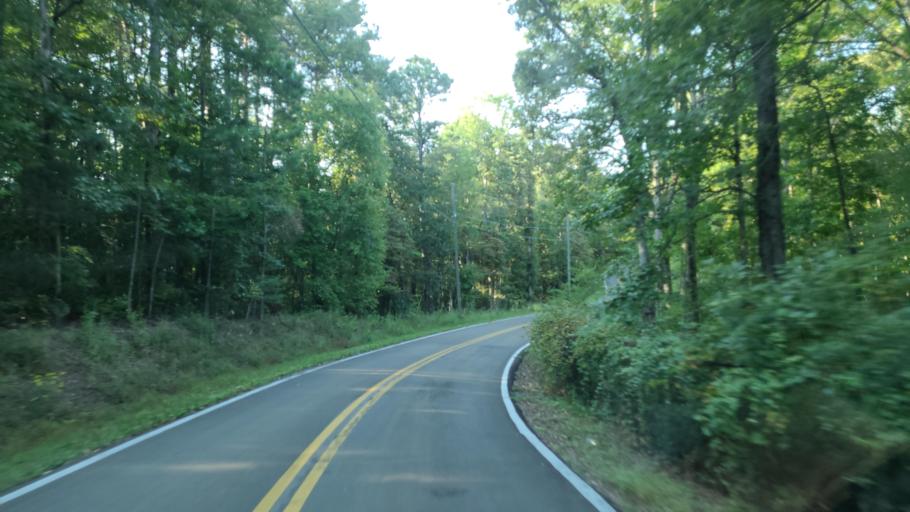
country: US
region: Georgia
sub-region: Pickens County
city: Nelson
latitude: 34.4069
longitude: -84.4145
